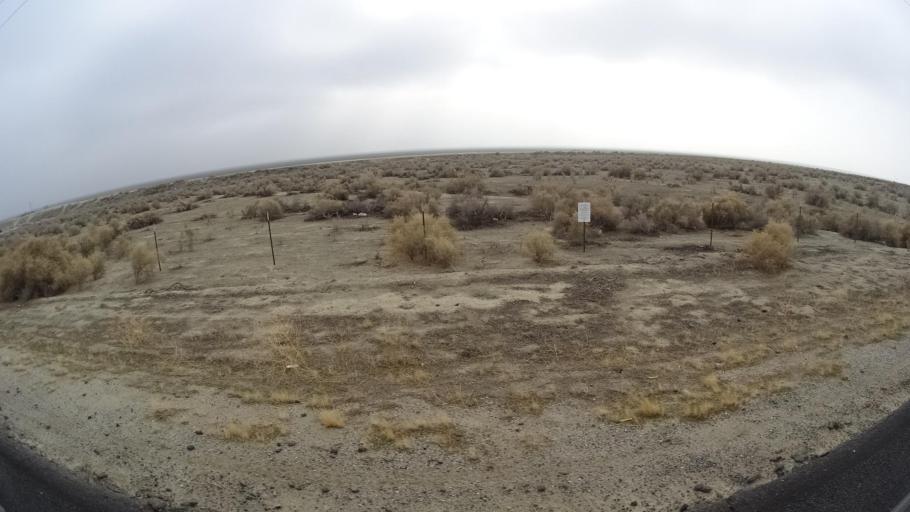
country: US
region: California
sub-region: Kern County
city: Ford City
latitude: 35.2342
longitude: -119.3350
